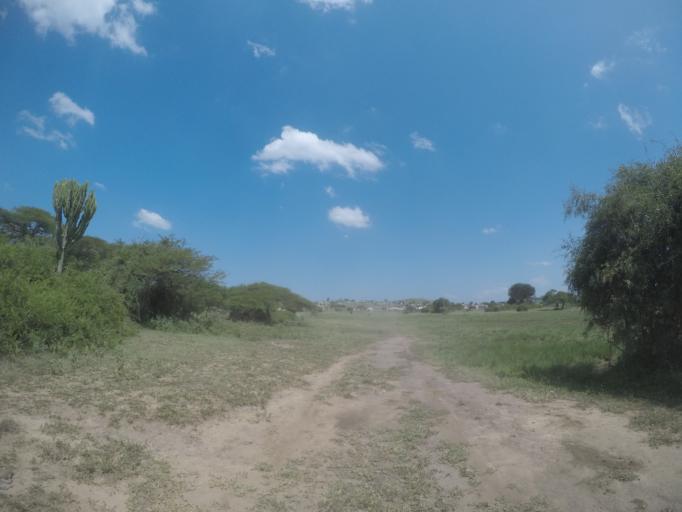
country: ZA
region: KwaZulu-Natal
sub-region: uThungulu District Municipality
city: Empangeni
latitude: -28.5860
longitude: 31.7394
